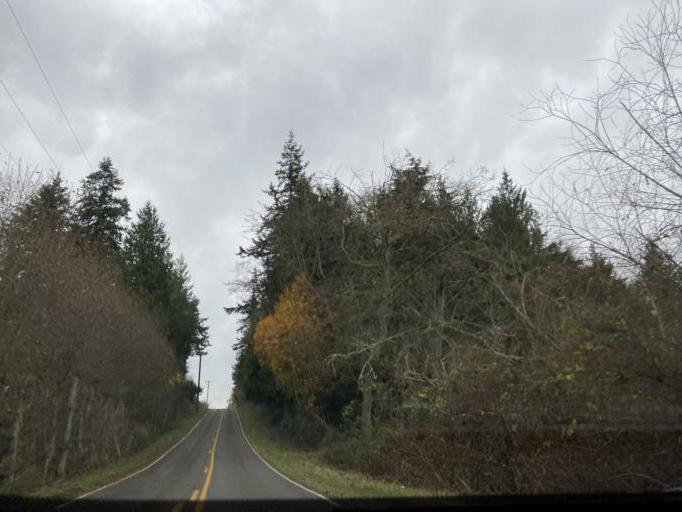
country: US
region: Washington
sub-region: Island County
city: Freeland
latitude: 48.0130
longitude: -122.5070
